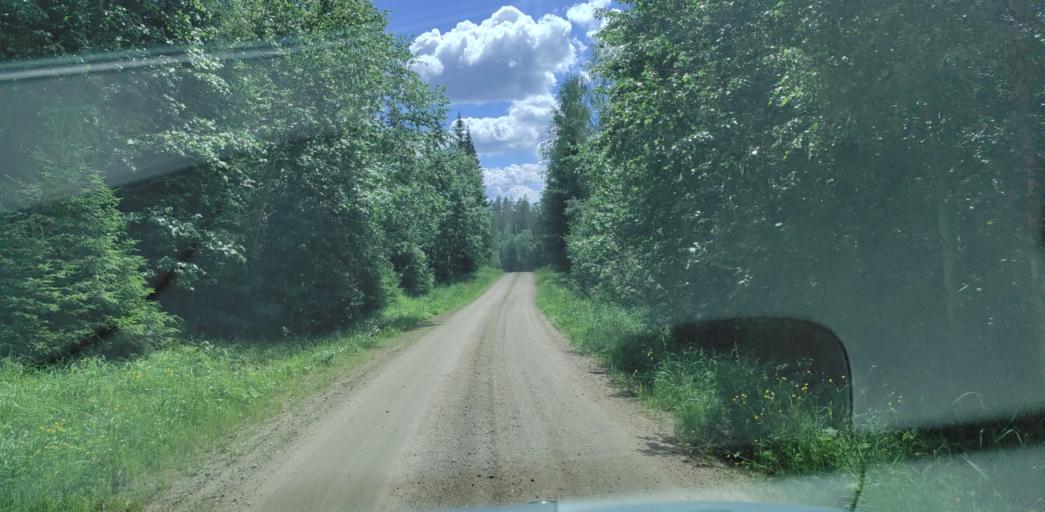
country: SE
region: Vaermland
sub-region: Hagfors Kommun
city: Ekshaerad
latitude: 60.0956
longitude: 13.3171
